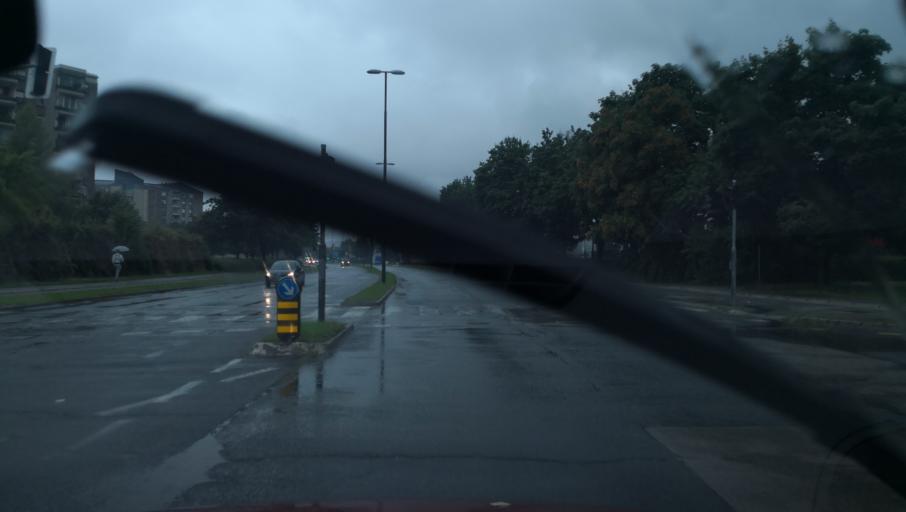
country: SI
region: Dol pri Ljubljani
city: Dol pri Ljubljani
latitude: 46.0560
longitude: 14.5614
